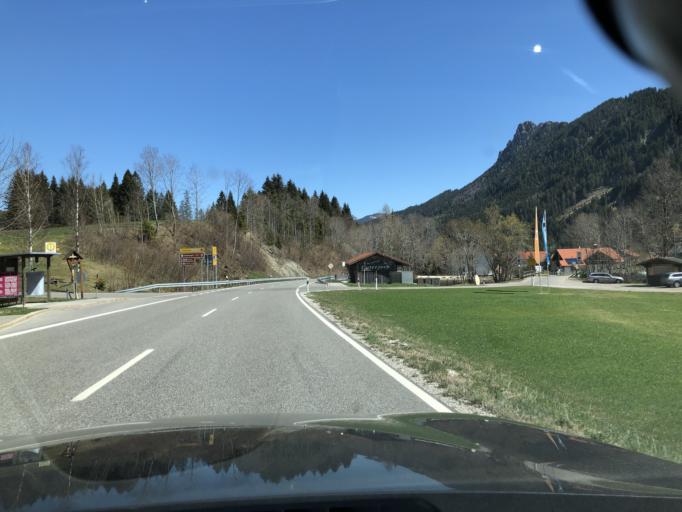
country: AT
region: Tyrol
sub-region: Politischer Bezirk Reutte
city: Schattwald
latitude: 47.5432
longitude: 10.4200
